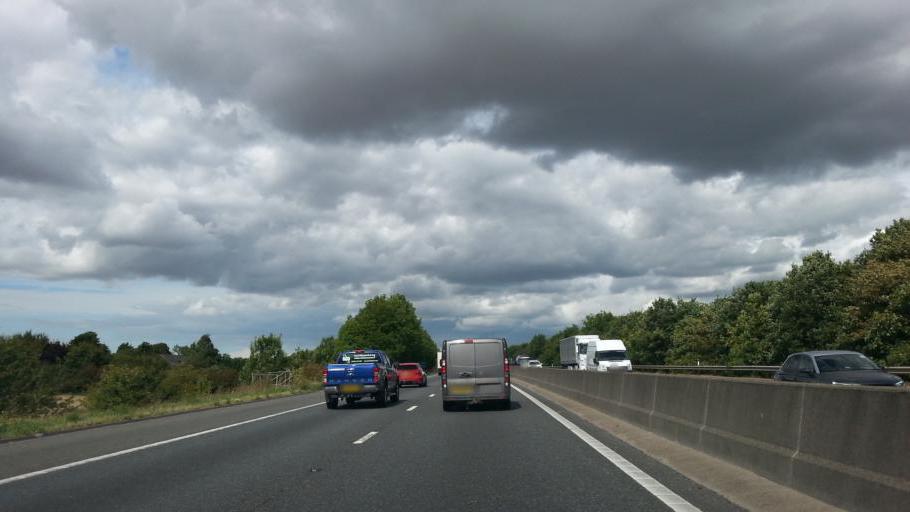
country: GB
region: England
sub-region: Essex
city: Elsenham
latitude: 51.9481
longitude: 0.2159
